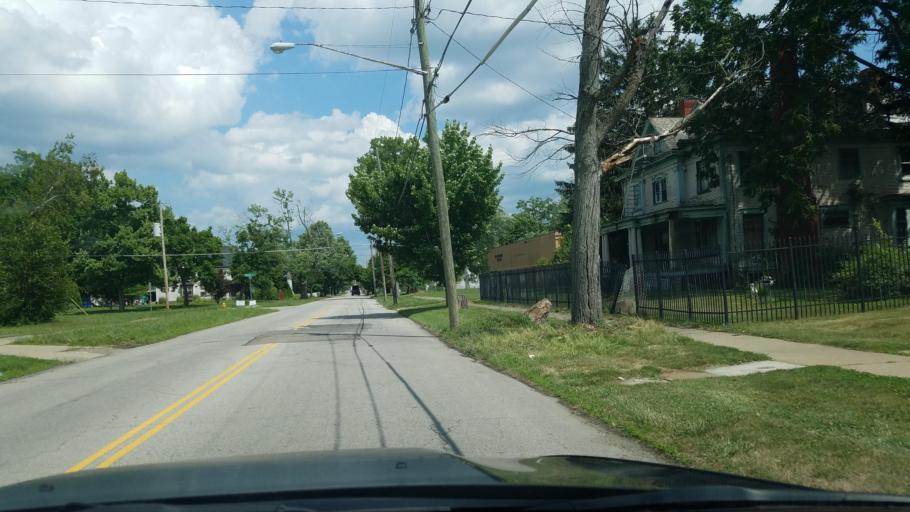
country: US
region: Ohio
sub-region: Trumbull County
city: Warren
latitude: 41.2419
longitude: -80.8170
